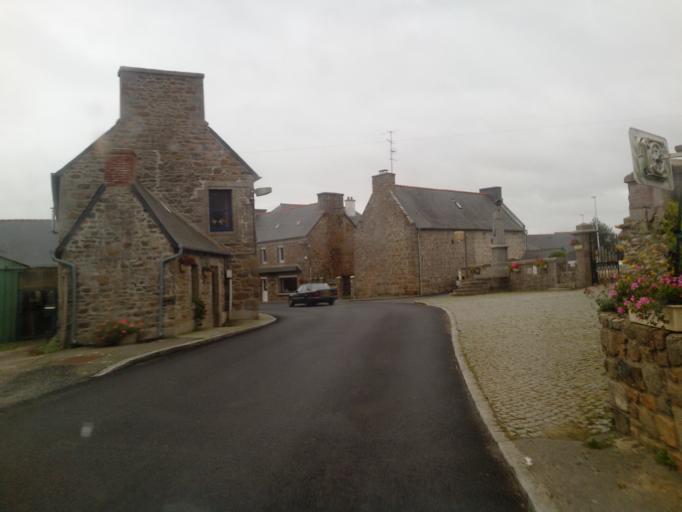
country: FR
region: Brittany
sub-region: Departement des Cotes-d'Armor
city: Pleubian
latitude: 48.8423
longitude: -3.1068
